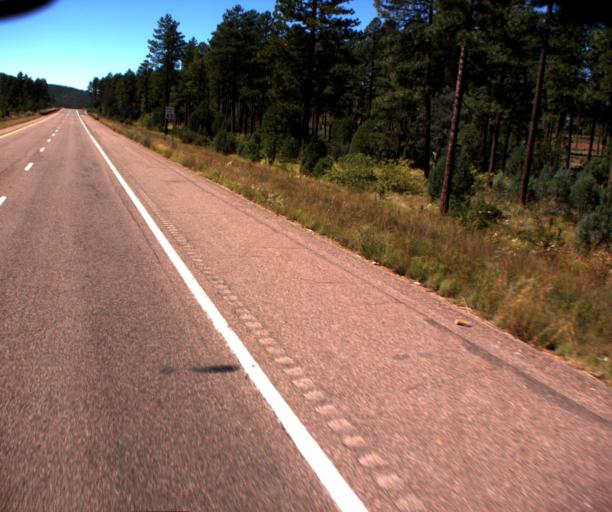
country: US
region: Arizona
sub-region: Gila County
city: Star Valley
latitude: 34.3131
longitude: -111.0064
